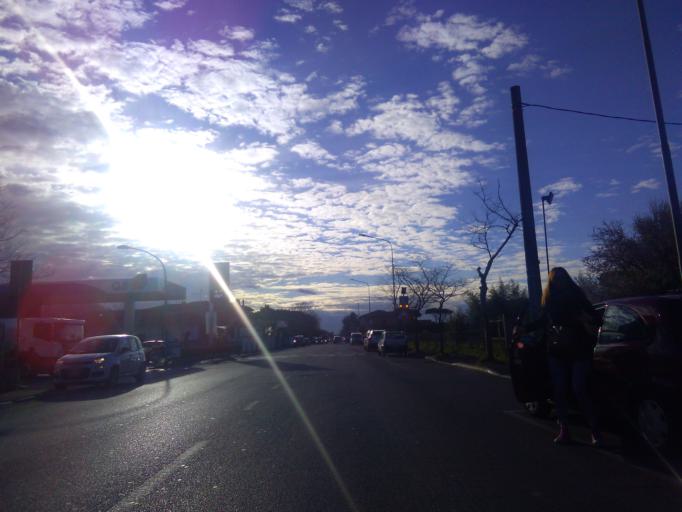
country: IT
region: Tuscany
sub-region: Provincia di Massa-Carrara
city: Marina di Carrara
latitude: 44.0534
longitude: 10.0425
